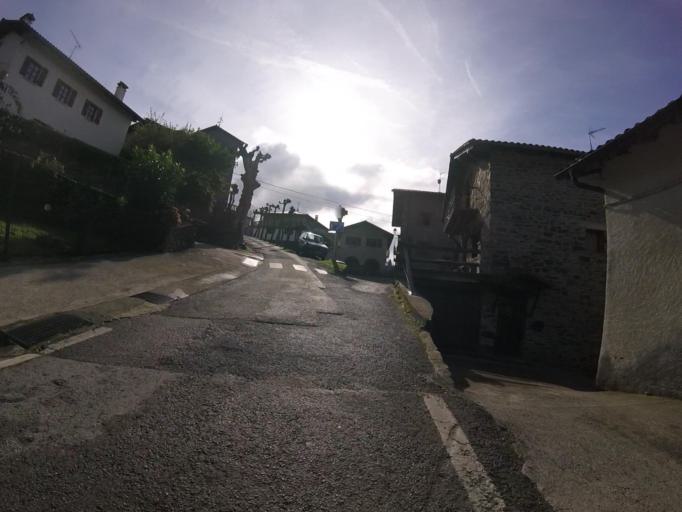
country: ES
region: Navarre
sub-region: Provincia de Navarra
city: Arano
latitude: 43.1998
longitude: -1.8951
